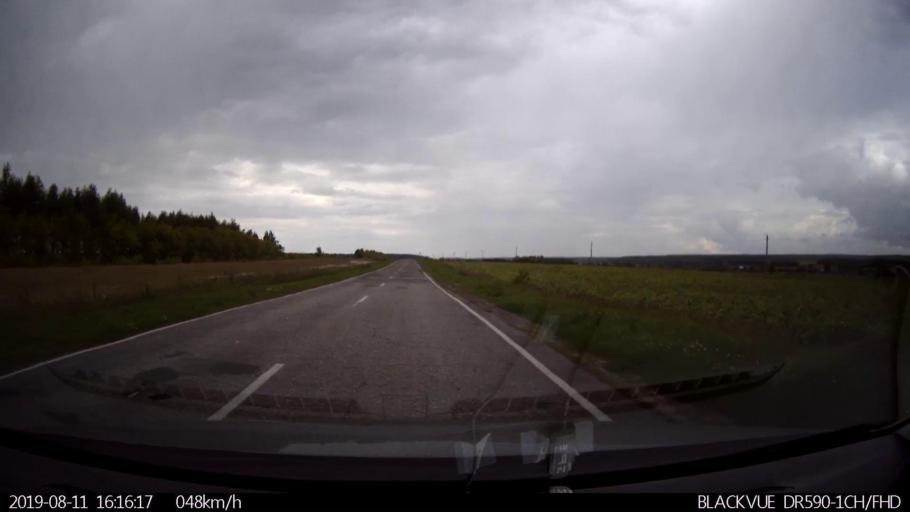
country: RU
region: Ulyanovsk
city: Mayna
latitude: 54.0399
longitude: 47.6222
